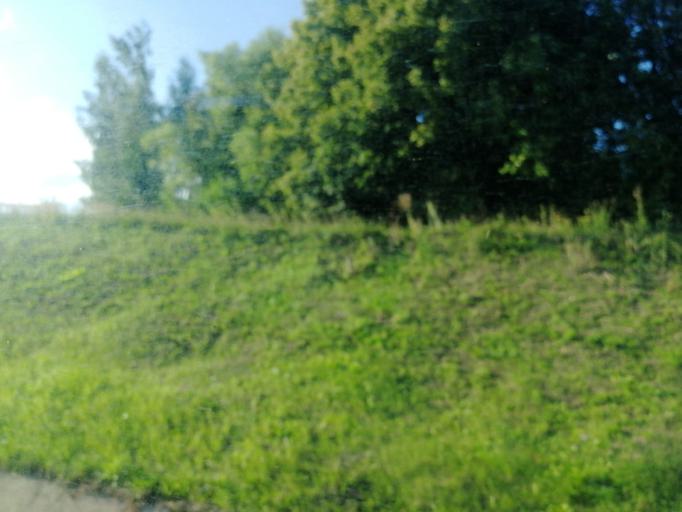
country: RU
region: Tula
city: Dubna
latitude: 54.2814
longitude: 37.1706
